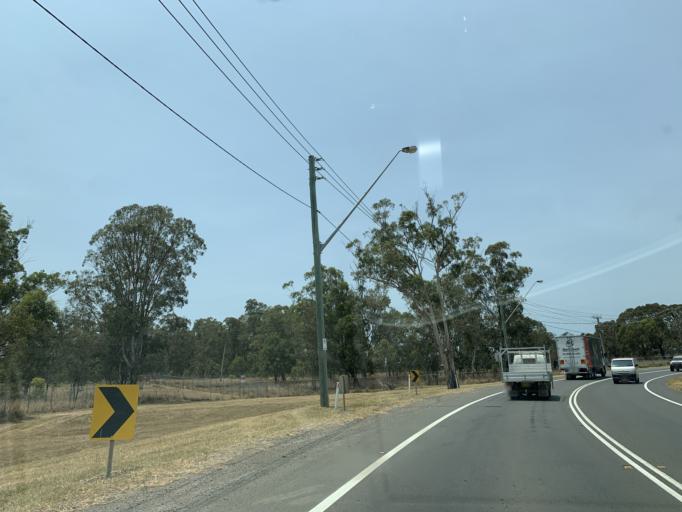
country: AU
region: New South Wales
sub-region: Fairfield
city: Horsley Park
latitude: -33.8227
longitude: 150.8700
